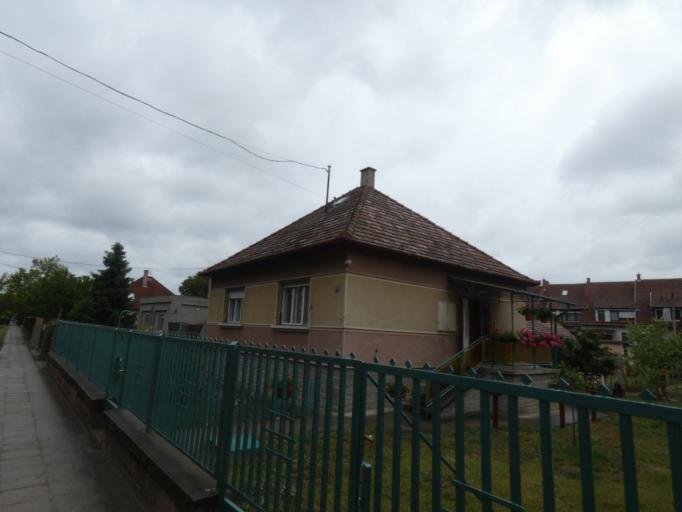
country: HU
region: Pest
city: Godollo
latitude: 47.5918
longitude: 19.3464
